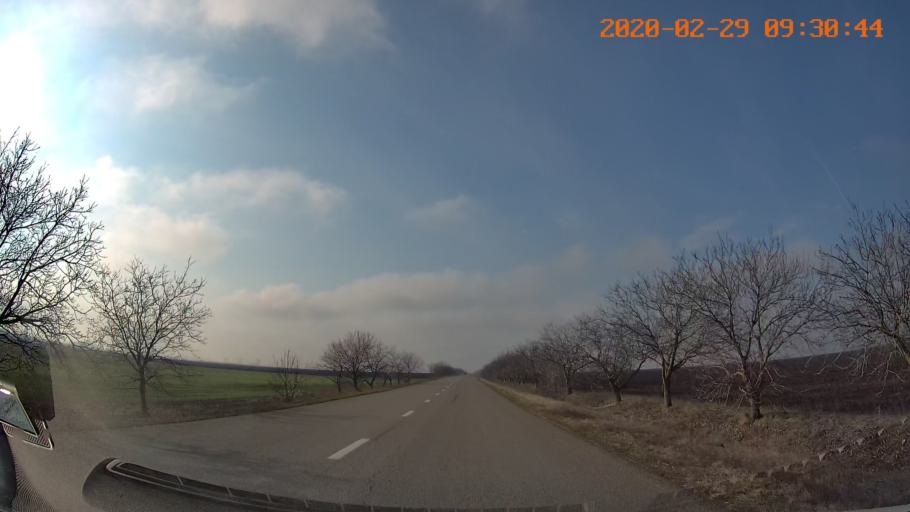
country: MD
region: Telenesti
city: Dnestrovsc
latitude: 46.6625
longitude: 29.9150
